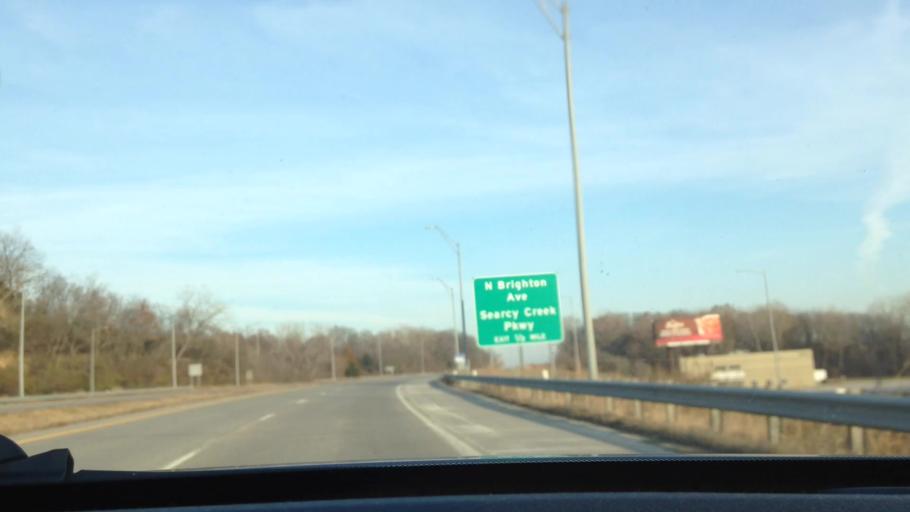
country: US
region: Missouri
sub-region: Clay County
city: North Kansas City
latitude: 39.1508
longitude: -94.5350
